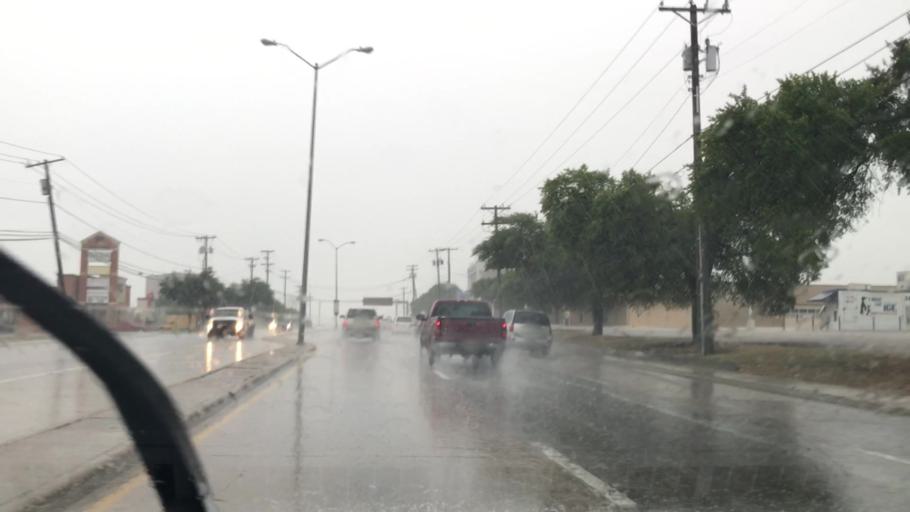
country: US
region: Texas
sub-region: Dallas County
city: Addison
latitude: 32.9297
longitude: -96.8036
